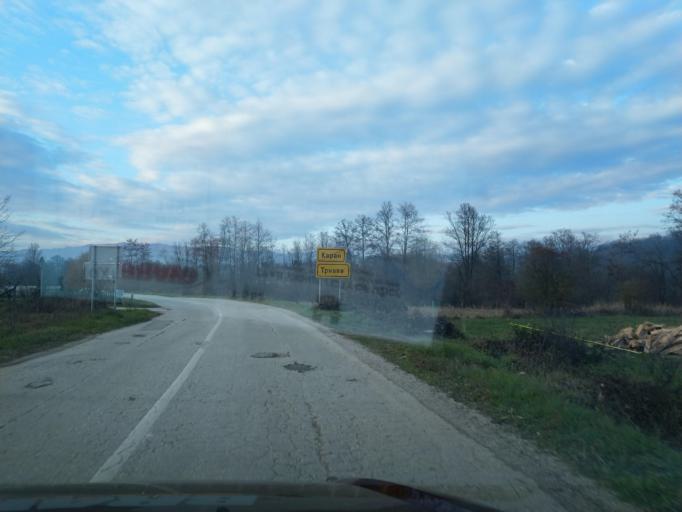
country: RS
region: Central Serbia
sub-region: Zlatiborski Okrug
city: Kosjeric
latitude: 43.9240
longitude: 19.9004
